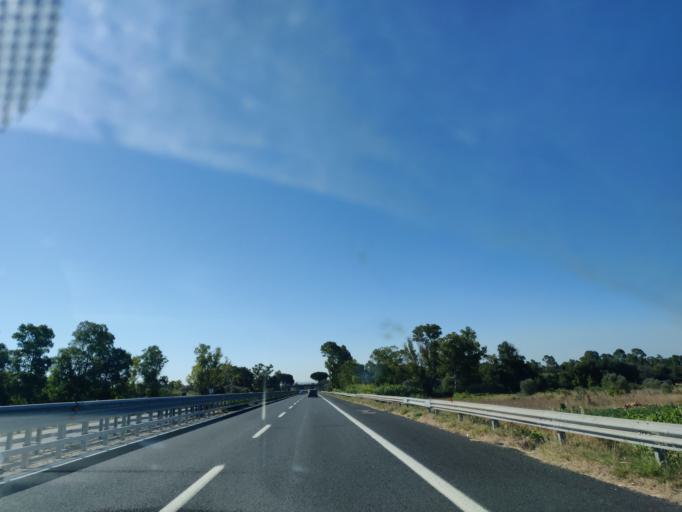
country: IT
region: Latium
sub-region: Citta metropolitana di Roma Capitale
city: Valcanneto
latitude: 41.9445
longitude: 12.1419
